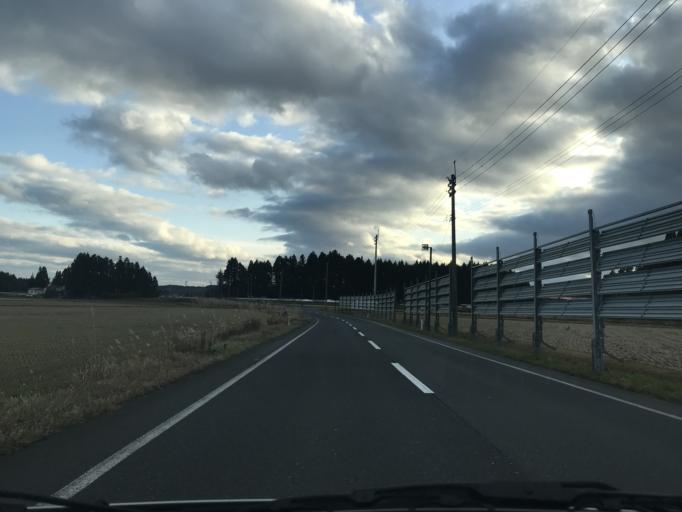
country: JP
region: Iwate
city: Mizusawa
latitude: 39.0816
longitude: 141.0514
